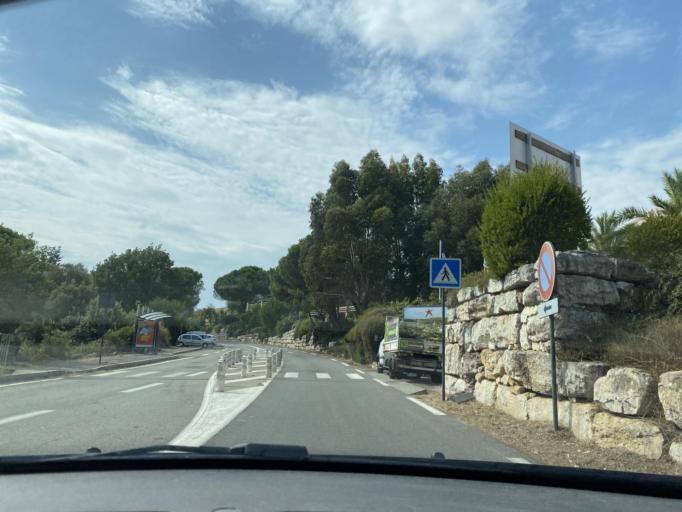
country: FR
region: Provence-Alpes-Cote d'Azur
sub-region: Departement des Alpes-Maritimes
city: Biot
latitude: 43.6279
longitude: 7.0525
